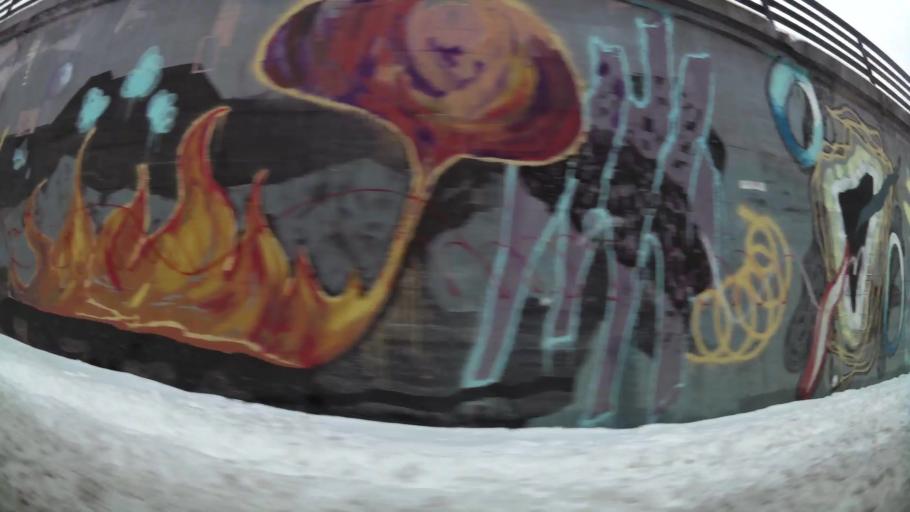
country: RS
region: Central Serbia
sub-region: Belgrade
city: Stari Grad
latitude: 44.8190
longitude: 20.4868
